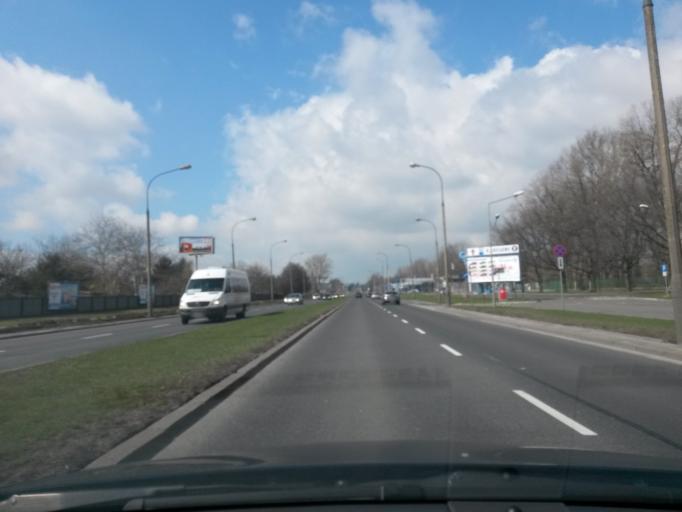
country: PL
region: Masovian Voivodeship
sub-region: Warszawa
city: Wlochy
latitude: 52.1865
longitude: 20.9697
